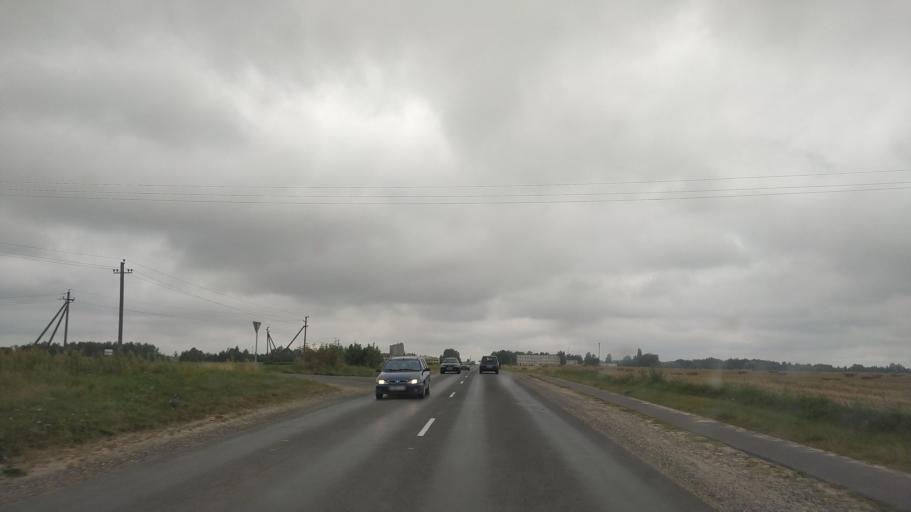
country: BY
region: Brest
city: Byaroza
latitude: 52.5481
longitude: 24.9493
